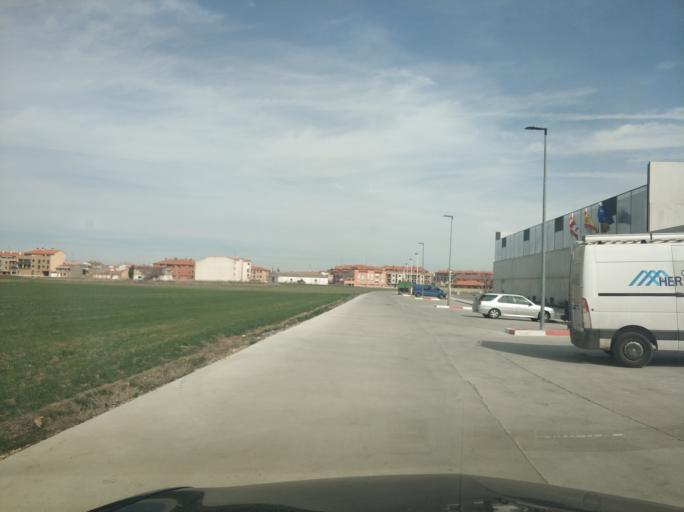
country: ES
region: Castille and Leon
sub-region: Provincia de Salamanca
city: Castellanos de Moriscos
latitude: 41.0151
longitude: -5.5939
